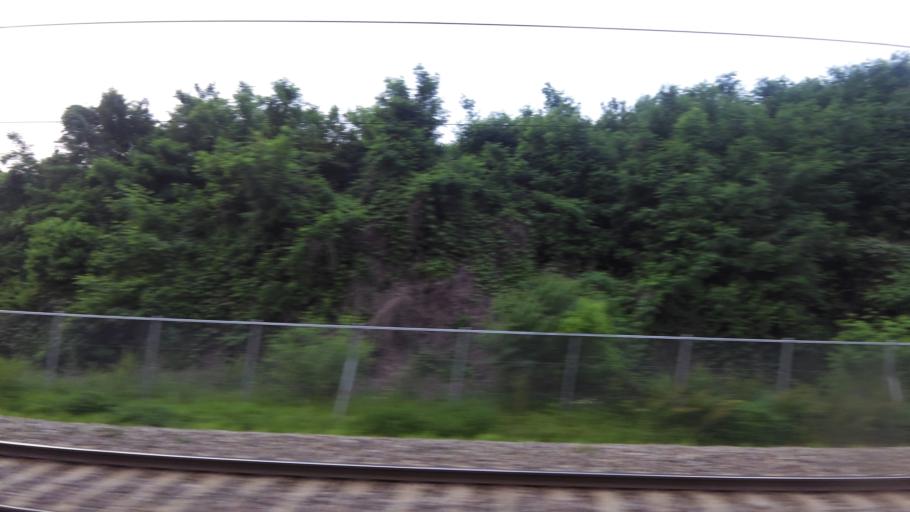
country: KR
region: Daejeon
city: Songgang-dong
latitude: 36.5418
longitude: 127.3368
